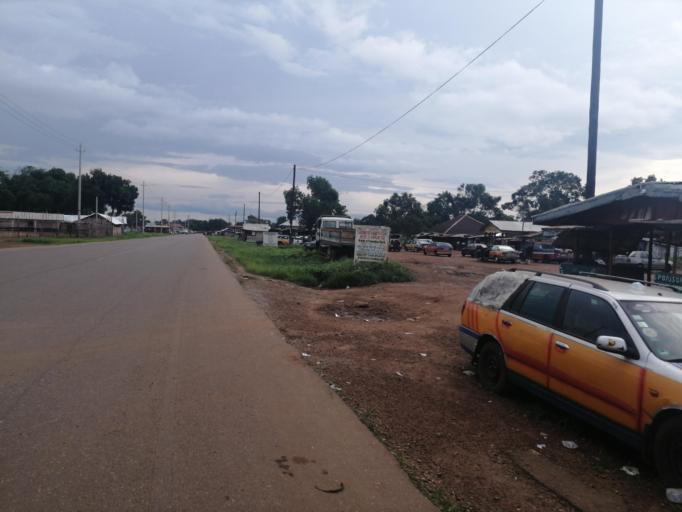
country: SL
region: Northern Province
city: Port Loko
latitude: 8.7763
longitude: -12.7851
